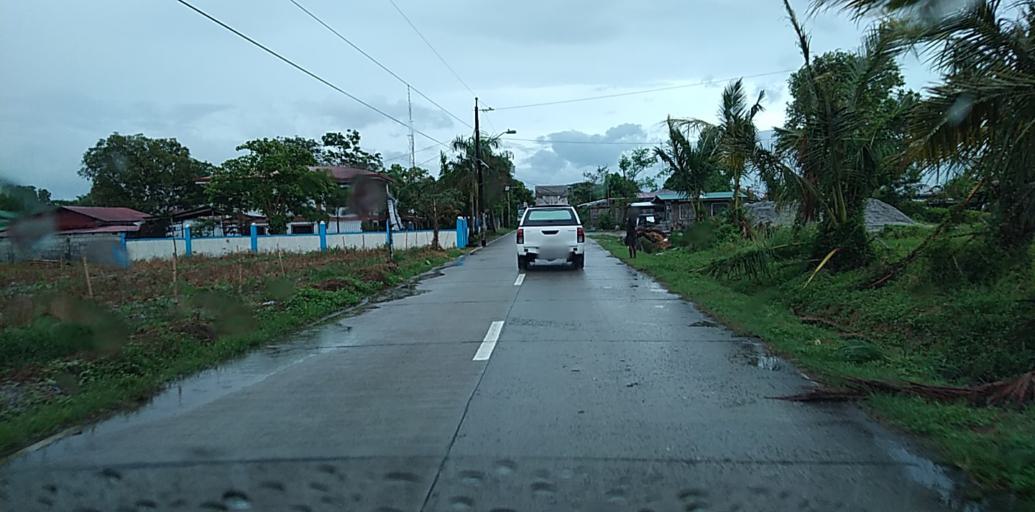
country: PH
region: Central Luzon
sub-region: Province of Pampanga
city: Salapungan
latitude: 15.1339
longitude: 120.9260
